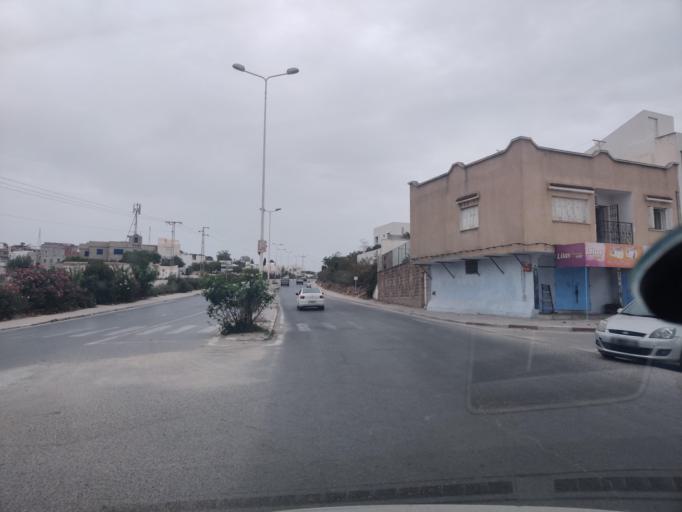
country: TN
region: Nabul
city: Al Hammamat
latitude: 36.4091
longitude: 10.6164
